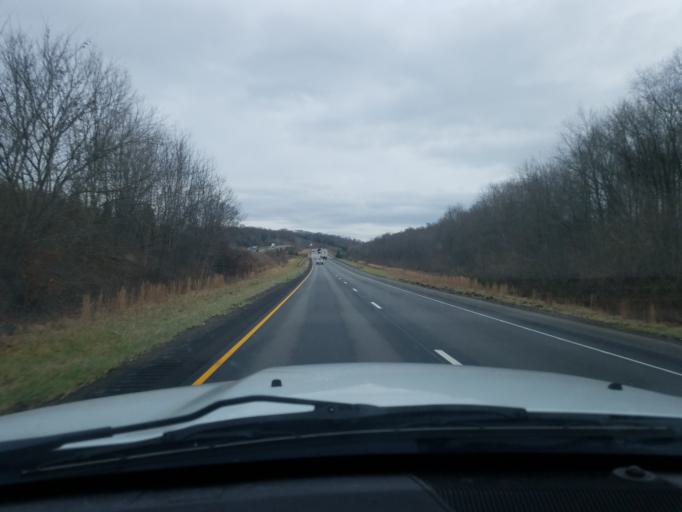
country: US
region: Indiana
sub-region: Dubois County
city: Ferdinand
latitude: 38.2056
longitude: -86.8057
